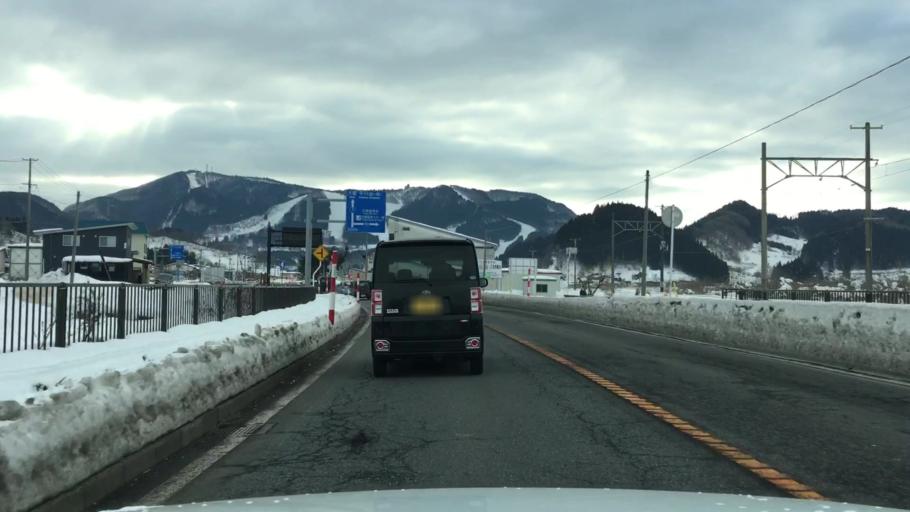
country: JP
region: Aomori
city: Hirosaki
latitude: 40.5303
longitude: 140.5546
